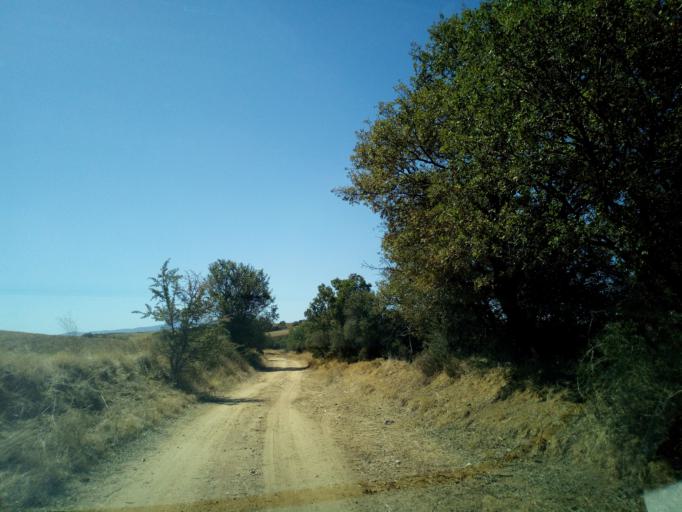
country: GR
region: Central Macedonia
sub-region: Nomos Thessalonikis
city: Kolchikon
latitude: 40.7435
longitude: 23.2501
